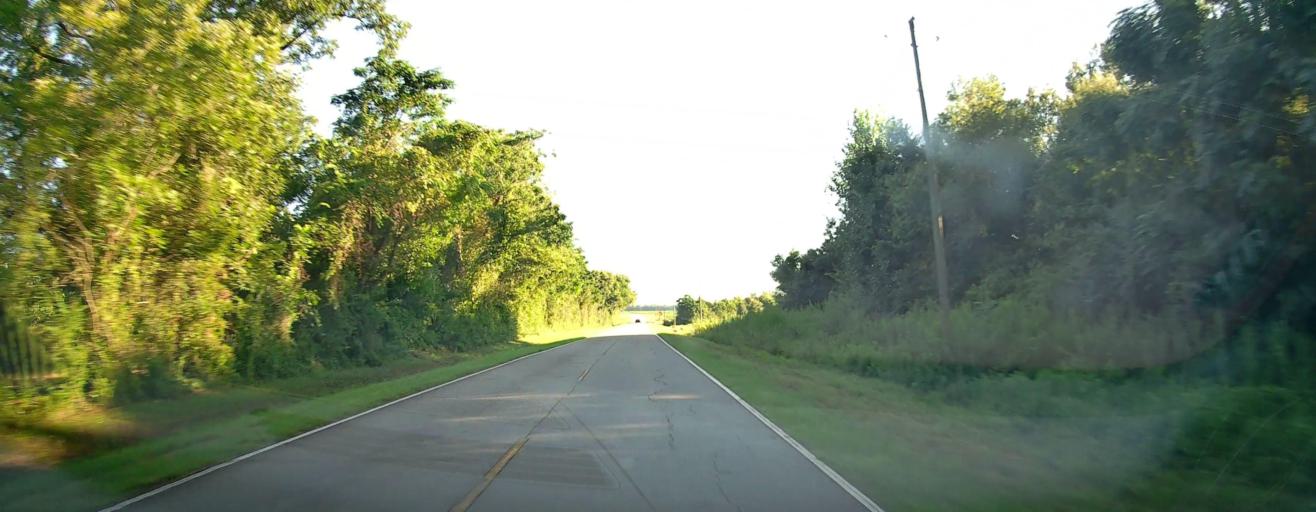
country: US
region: Georgia
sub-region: Bleckley County
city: Cochran
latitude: 32.3881
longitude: -83.4557
